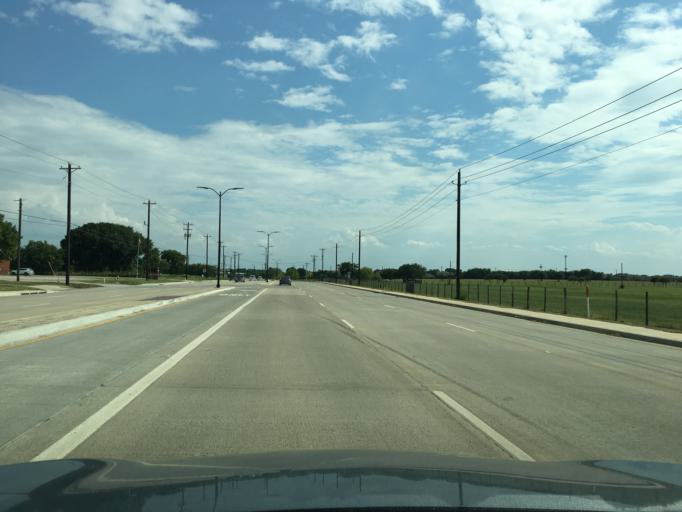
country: US
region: Texas
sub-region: Denton County
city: Oak Point
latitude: 33.1717
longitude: -96.9771
